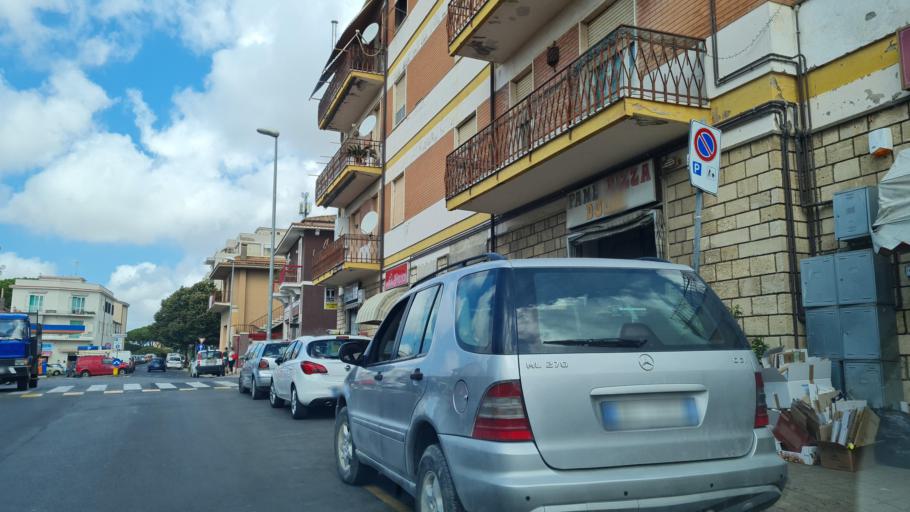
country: IT
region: Latium
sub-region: Provincia di Viterbo
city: Tarquinia
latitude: 42.2510
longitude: 11.7643
